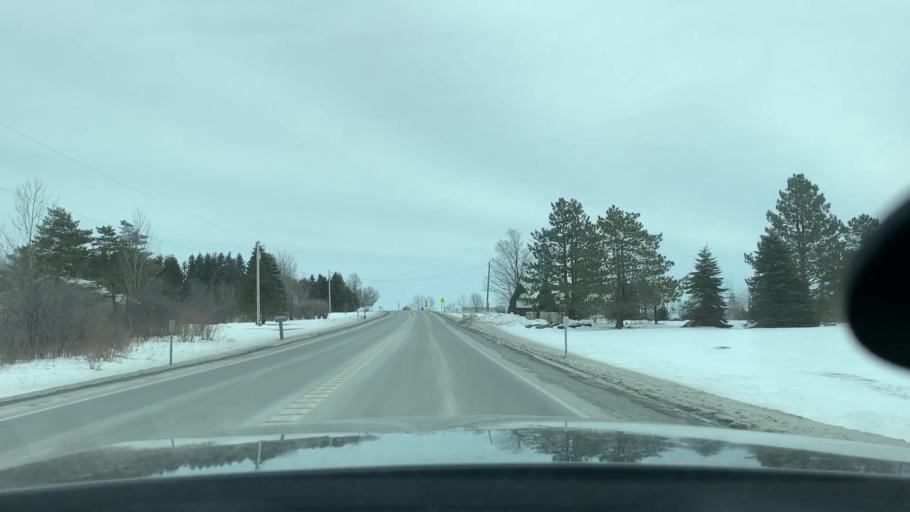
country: US
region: New York
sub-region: Oneida County
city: Utica
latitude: 43.0322
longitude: -75.1762
